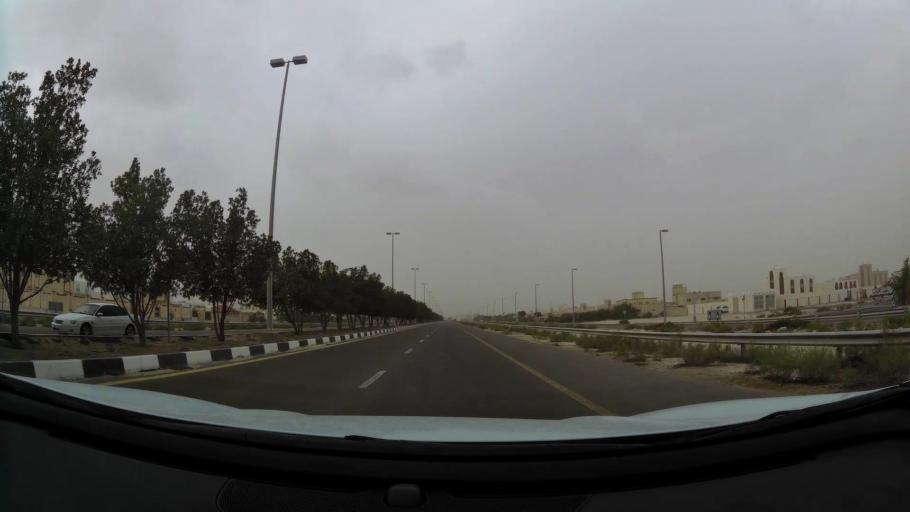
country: AE
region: Abu Dhabi
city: Abu Dhabi
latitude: 24.3910
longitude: 54.7119
